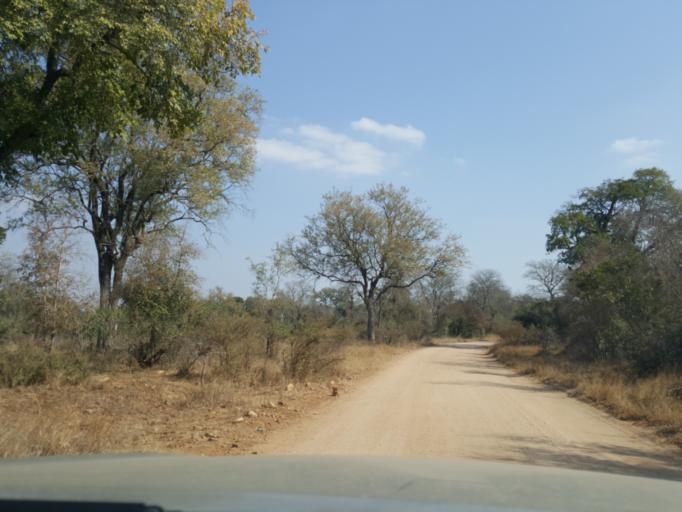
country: ZA
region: Mpumalanga
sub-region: Ehlanzeni District
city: Komatipoort
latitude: -25.2895
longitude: 31.7692
